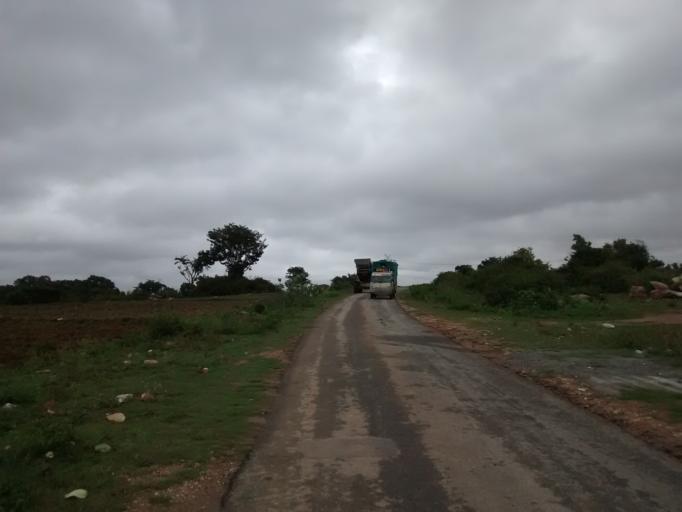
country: IN
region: Karnataka
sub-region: Hassan
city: Hassan
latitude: 12.9389
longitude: 76.1683
